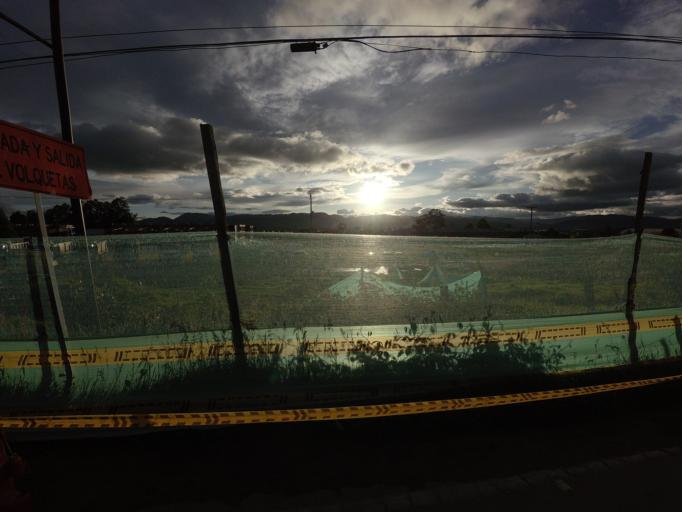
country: CO
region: Cundinamarca
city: Chia
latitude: 4.8339
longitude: -74.0291
